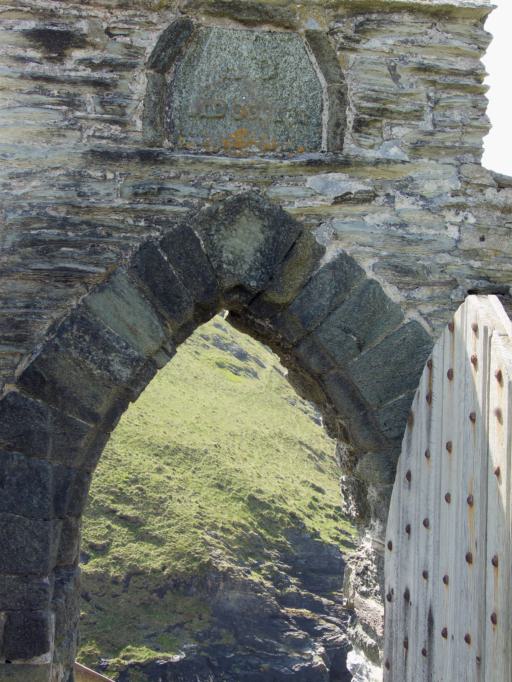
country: GB
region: England
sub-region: Cornwall
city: Tintagel
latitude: 50.6681
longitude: -4.7596
